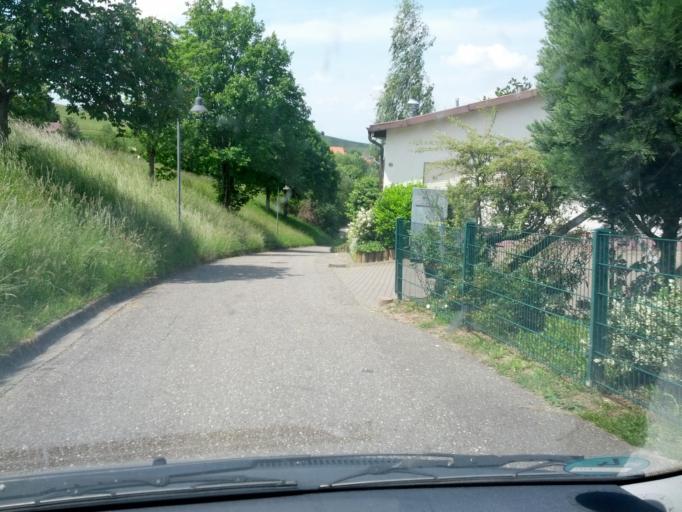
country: DE
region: Baden-Wuerttemberg
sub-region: Freiburg Region
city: Ebringen
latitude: 47.9542
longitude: 7.7757
